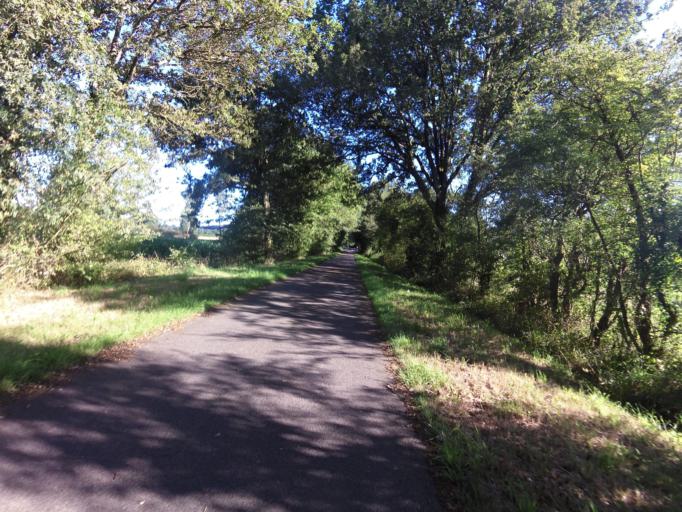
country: FR
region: Brittany
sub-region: Departement du Morbihan
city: Malestroit
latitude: 47.8270
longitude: -2.4198
